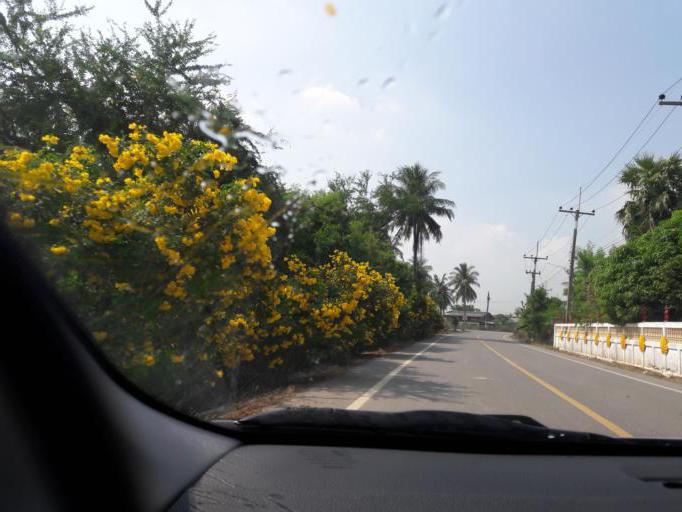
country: TH
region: Ang Thong
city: Ang Thong
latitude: 14.5714
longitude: 100.4212
